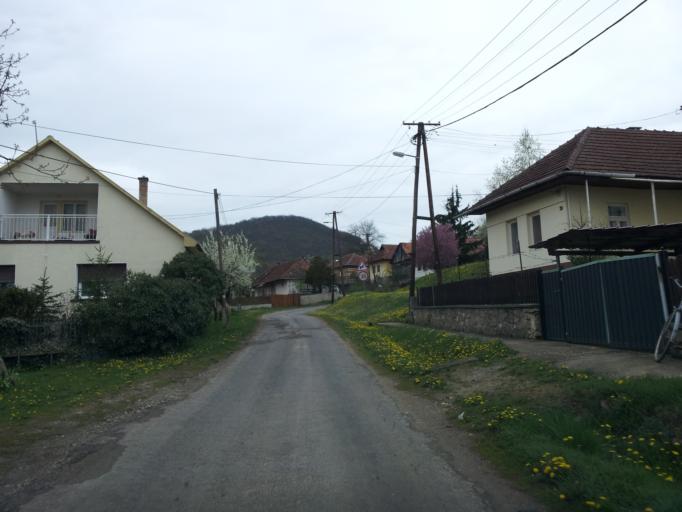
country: HU
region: Borsod-Abauj-Zemplen
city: Szendro
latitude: 48.5243
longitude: 20.6734
